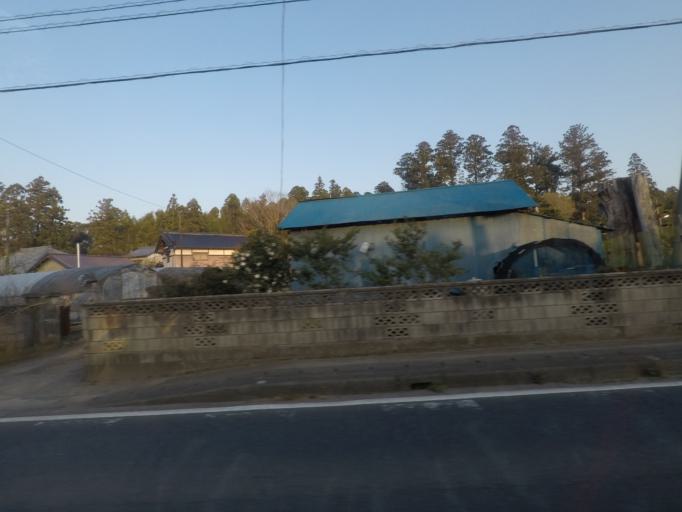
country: JP
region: Chiba
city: Narita
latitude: 35.8257
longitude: 140.4108
